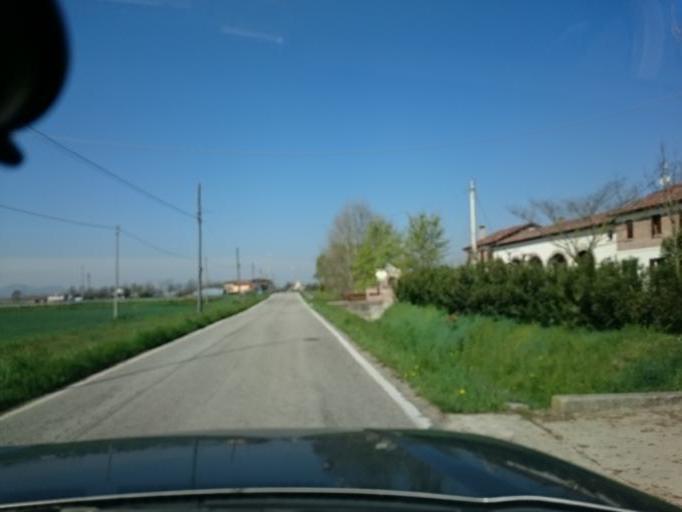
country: IT
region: Veneto
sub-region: Provincia di Padova
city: Ponte San Nicolo
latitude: 45.3456
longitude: 11.9207
